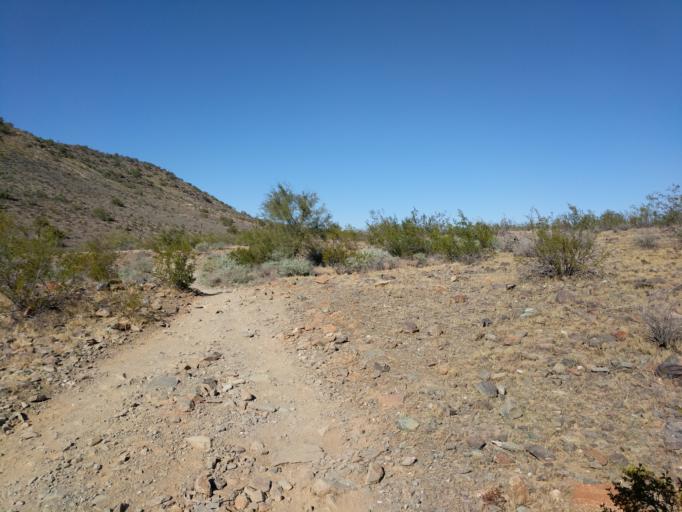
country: US
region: Arizona
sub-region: Maricopa County
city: Glendale
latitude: 33.5908
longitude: -112.0775
